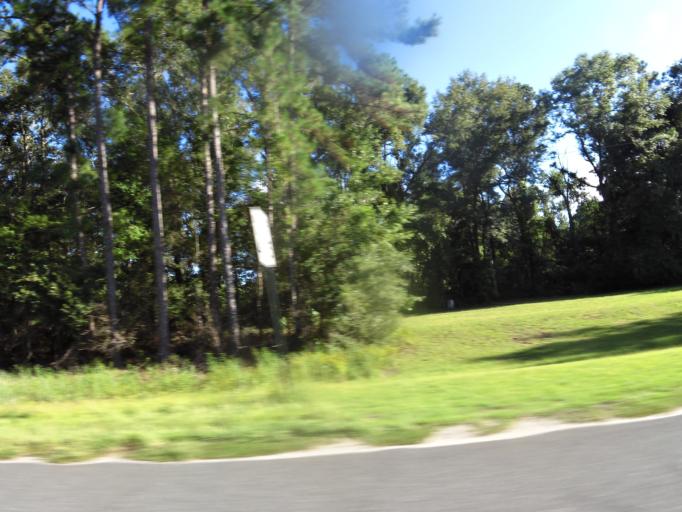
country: US
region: Florida
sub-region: Wakulla County
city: Crawfordville
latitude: 30.0639
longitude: -84.5170
